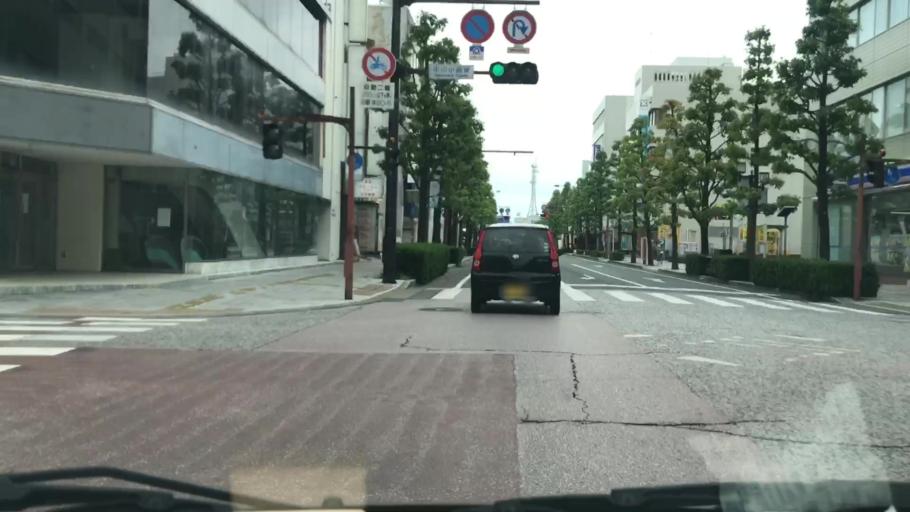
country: JP
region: Saga Prefecture
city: Saga-shi
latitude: 33.2533
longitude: 130.3000
